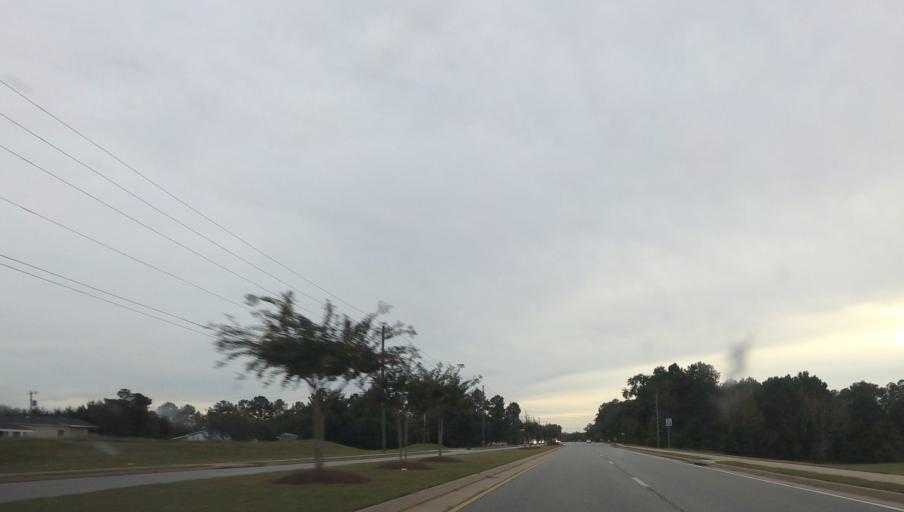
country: US
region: Georgia
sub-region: Houston County
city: Centerville
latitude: 32.5370
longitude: -83.6602
